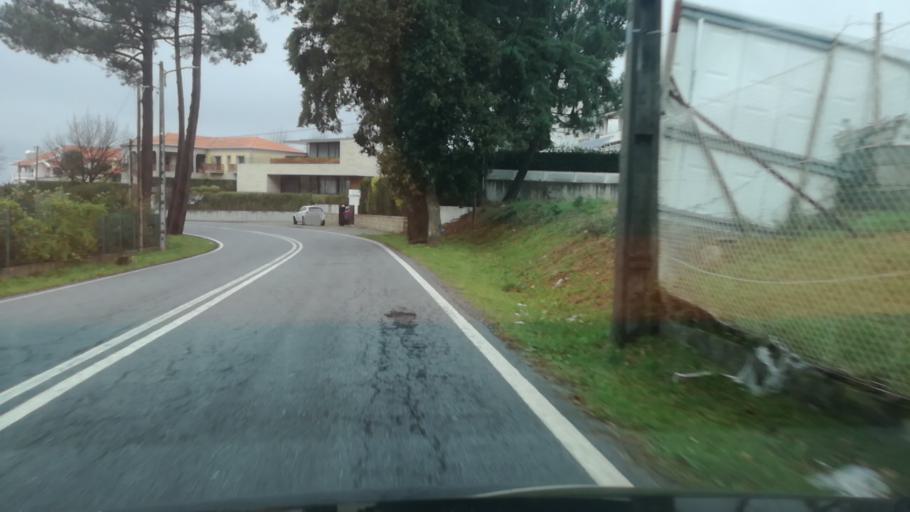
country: PT
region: Braga
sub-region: Braga
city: Braga
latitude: 41.5326
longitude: -8.3975
